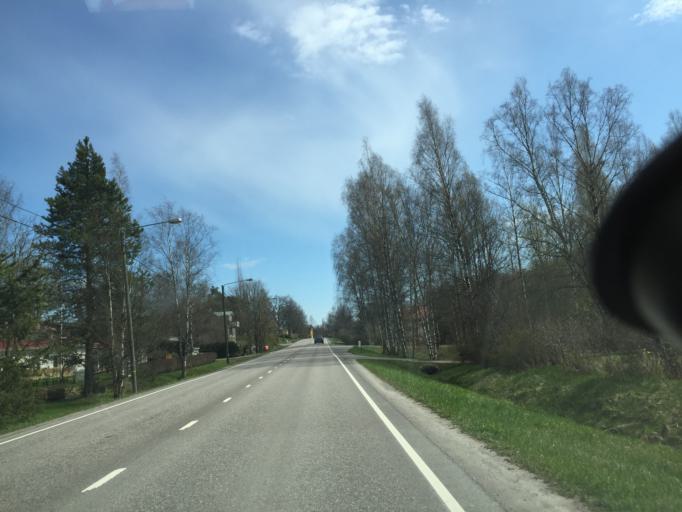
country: FI
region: Uusimaa
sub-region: Raaseporin
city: Ekenaes
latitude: 59.9886
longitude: 23.4151
